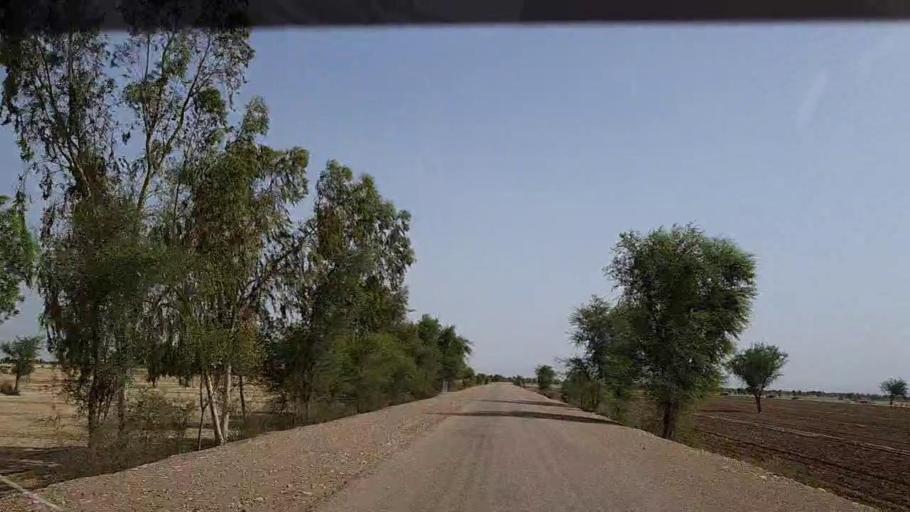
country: PK
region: Sindh
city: Johi
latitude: 26.6542
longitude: 67.5052
